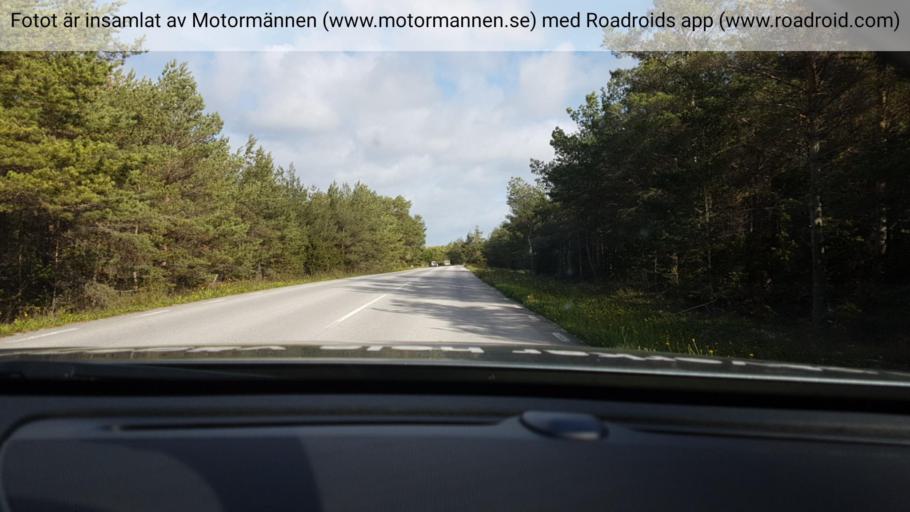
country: SE
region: Gotland
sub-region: Gotland
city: Slite
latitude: 57.8761
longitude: 19.0856
